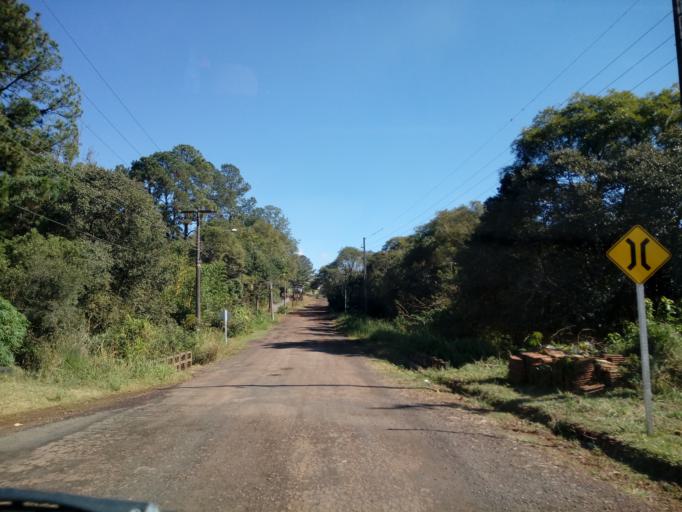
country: BR
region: Santa Catarina
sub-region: Chapeco
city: Chapeco
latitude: -27.0964
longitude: -52.6565
